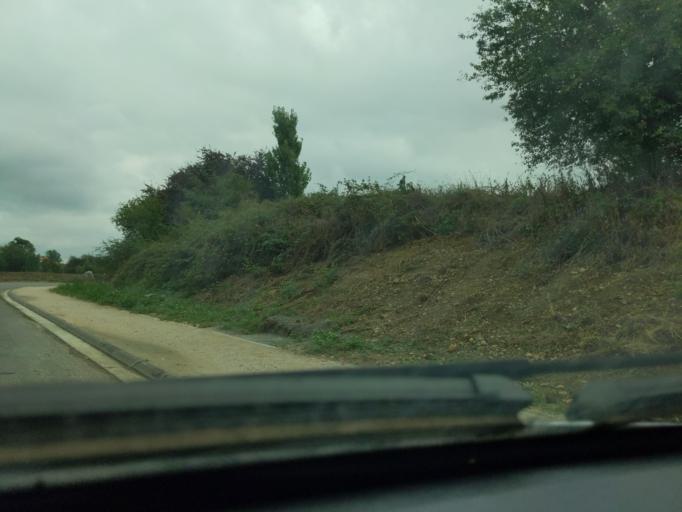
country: FR
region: Midi-Pyrenees
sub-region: Departement de la Haute-Garonne
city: Cugnaux
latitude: 43.5740
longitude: 1.3678
